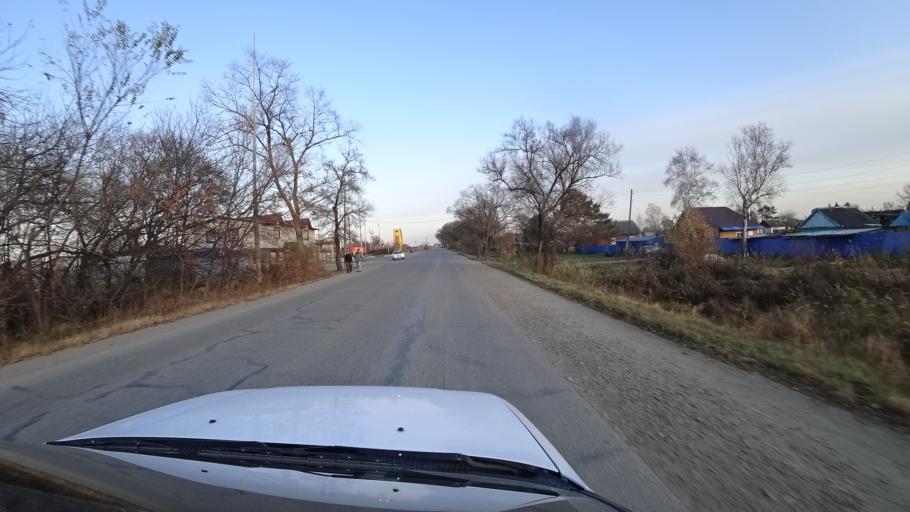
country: RU
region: Primorskiy
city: Dal'nerechensk
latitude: 45.9367
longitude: 133.8157
